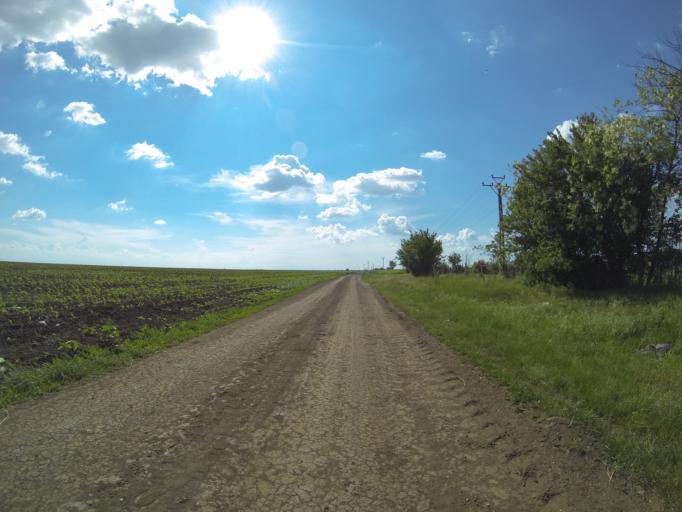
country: RO
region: Dolj
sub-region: Comuna Segarcea
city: Segarcea
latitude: 44.0779
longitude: 23.7415
